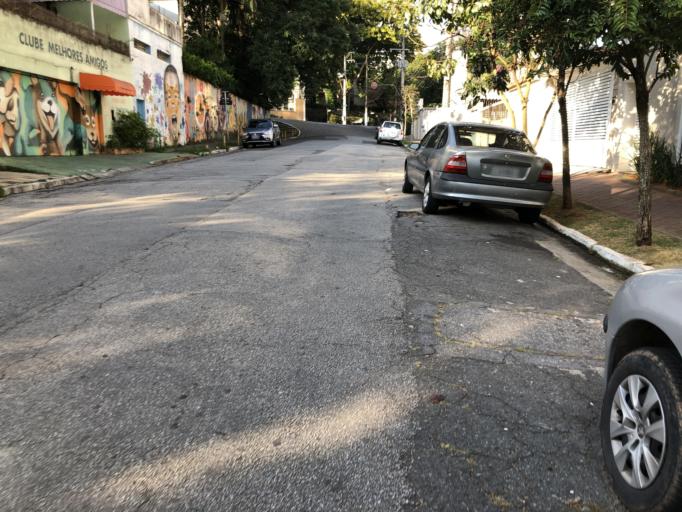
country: BR
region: Sao Paulo
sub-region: Sao Paulo
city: Sao Paulo
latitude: -23.6138
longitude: -46.6356
